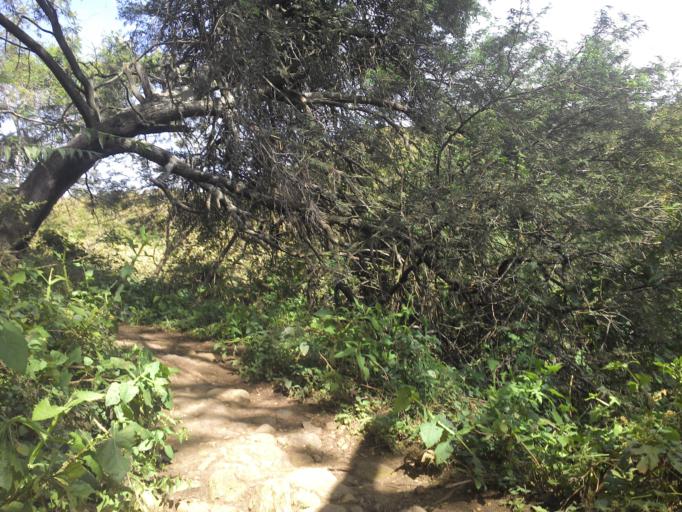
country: MX
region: Jalisco
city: Teuchitlan
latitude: 20.6954
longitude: -103.8350
